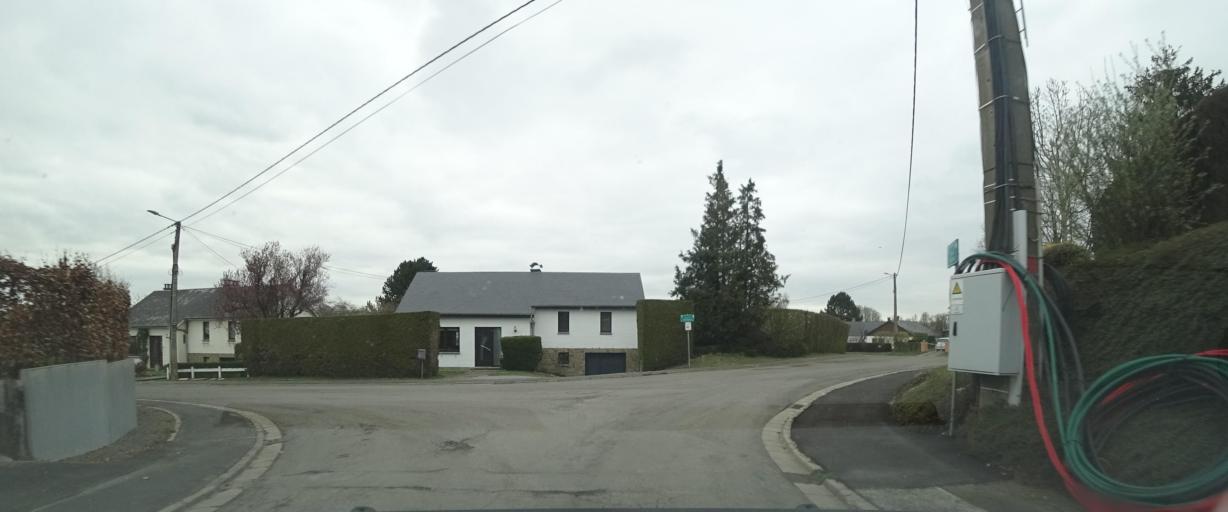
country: BE
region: Wallonia
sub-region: Province du Luxembourg
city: Marche-en-Famenne
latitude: 50.2232
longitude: 5.3527
